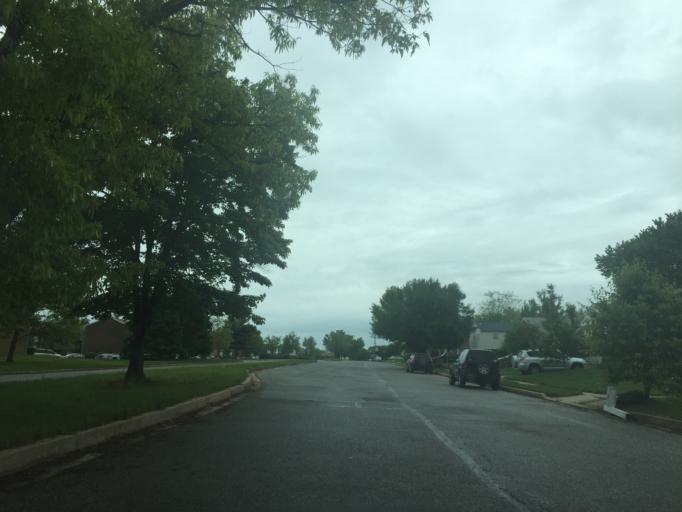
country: US
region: Maryland
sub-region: Baltimore County
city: Perry Hall
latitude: 39.4067
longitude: -76.4622
